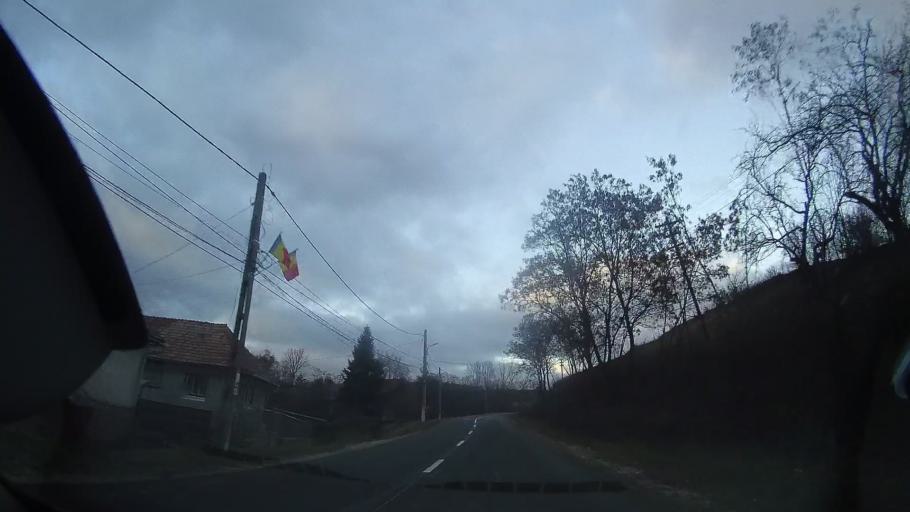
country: RO
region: Cluj
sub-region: Comuna Manastireni
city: Manastireni
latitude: 46.7833
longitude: 23.0893
